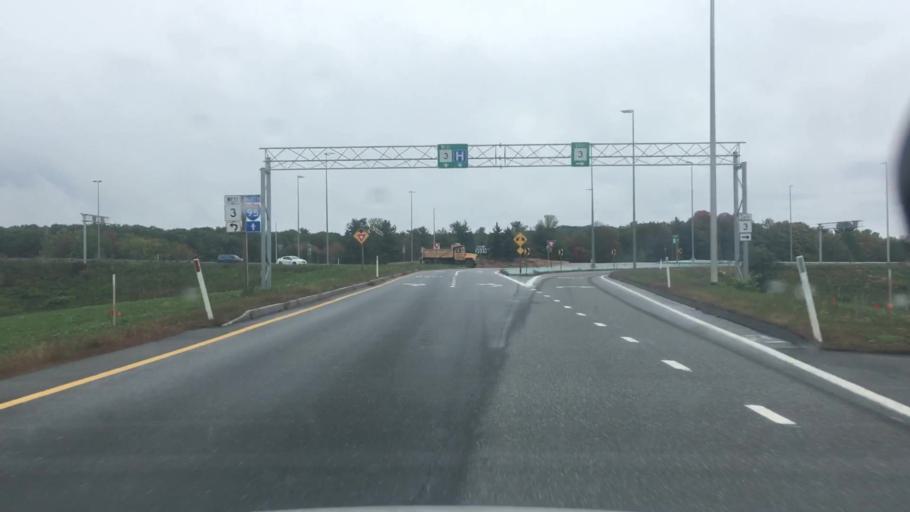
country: US
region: Maine
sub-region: Kennebec County
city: Augusta
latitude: 44.3528
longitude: -69.7822
